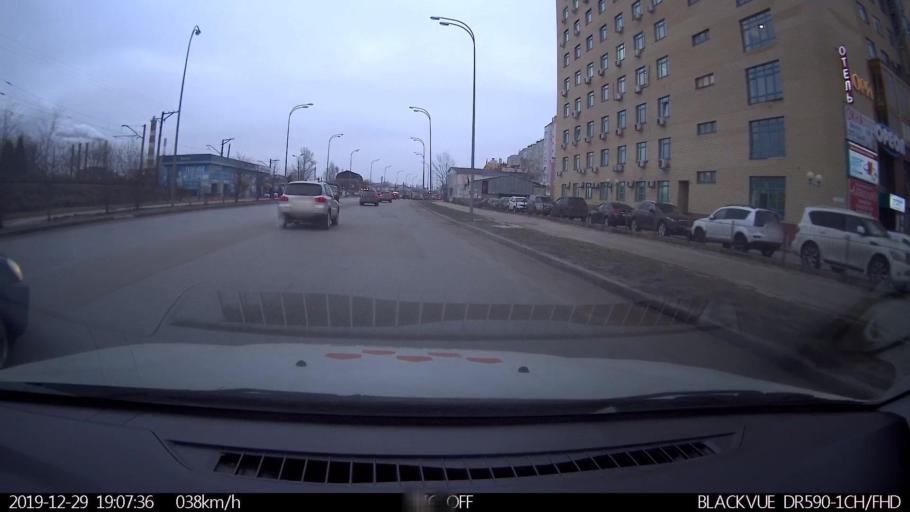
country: RU
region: Nizjnij Novgorod
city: Neklyudovo
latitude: 56.3547
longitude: 43.8680
